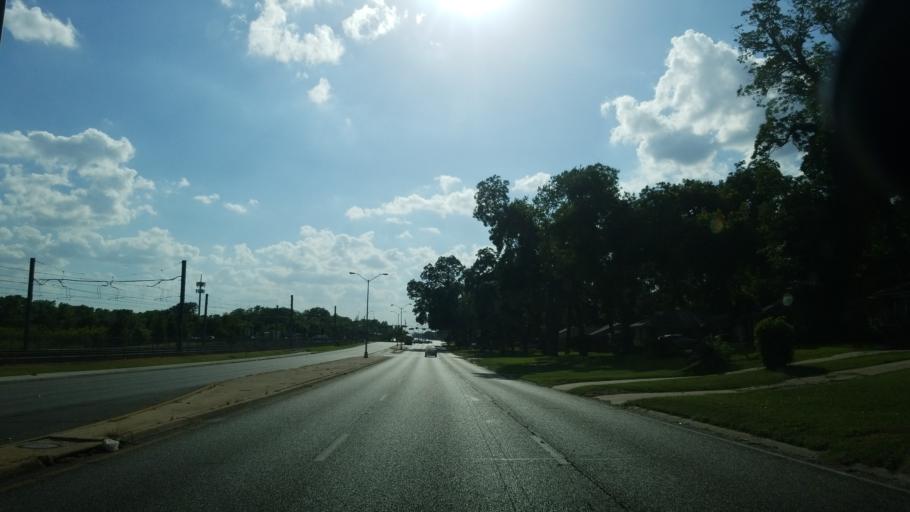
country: US
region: Texas
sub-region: Dallas County
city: Dallas
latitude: 32.7657
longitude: -96.7165
